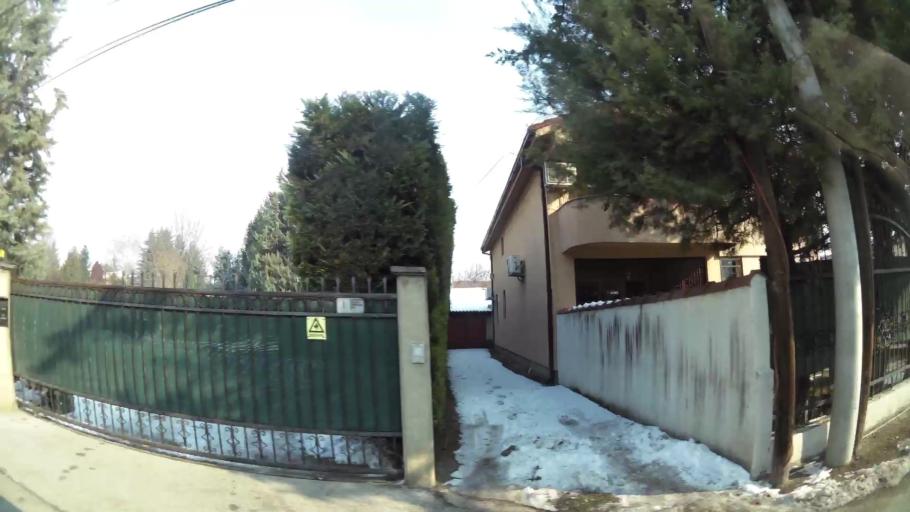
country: MK
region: Suto Orizari
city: Suto Orizare
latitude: 42.0161
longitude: 21.3868
